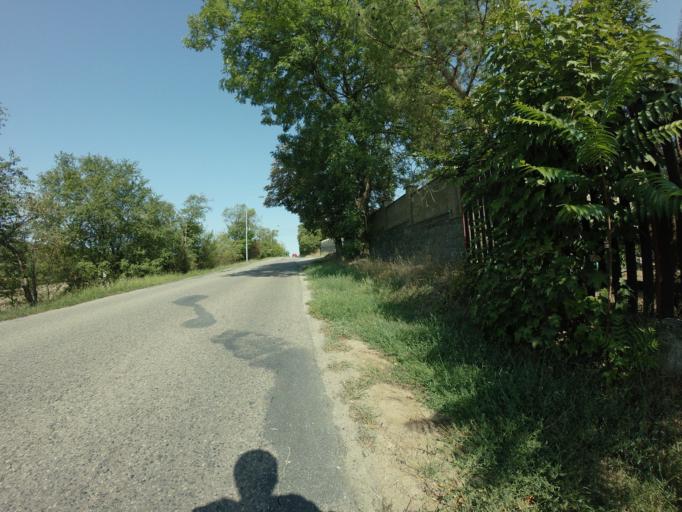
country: CZ
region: Central Bohemia
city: Tynec nad Sazavou
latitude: 49.8447
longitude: 14.5579
